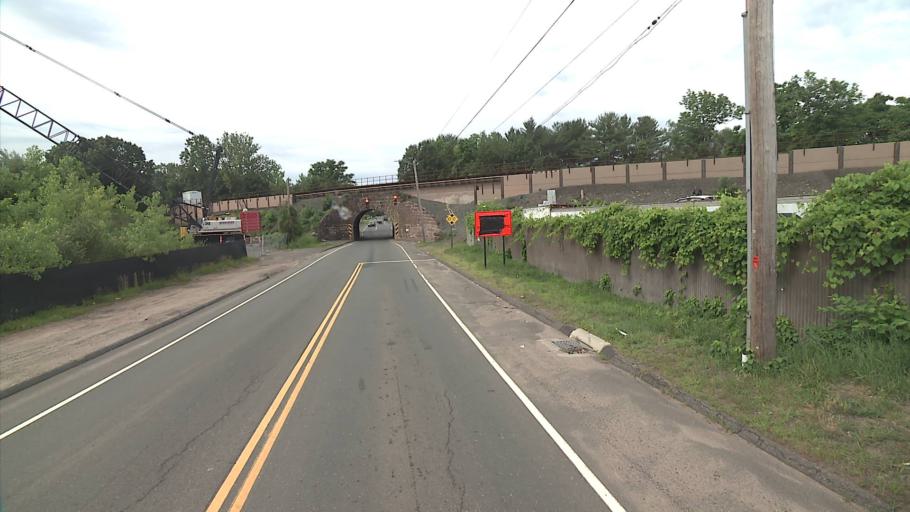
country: US
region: Connecticut
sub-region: New Haven County
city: Meriden
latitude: 41.4986
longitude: -72.8140
